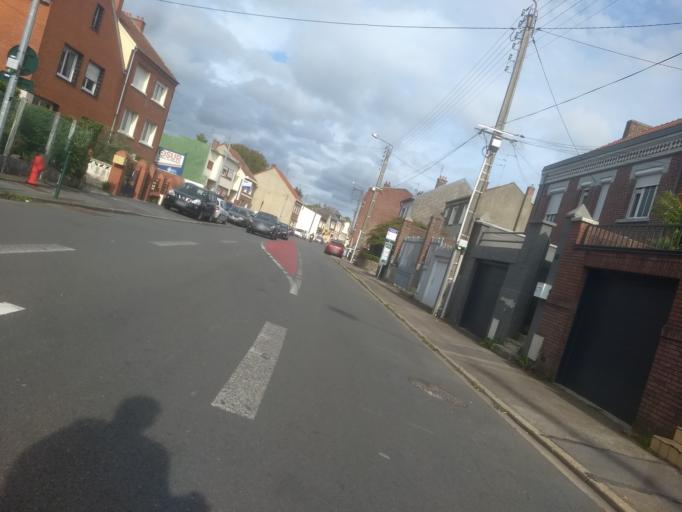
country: FR
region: Nord-Pas-de-Calais
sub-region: Departement du Pas-de-Calais
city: Achicourt
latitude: 50.2799
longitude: 2.7664
